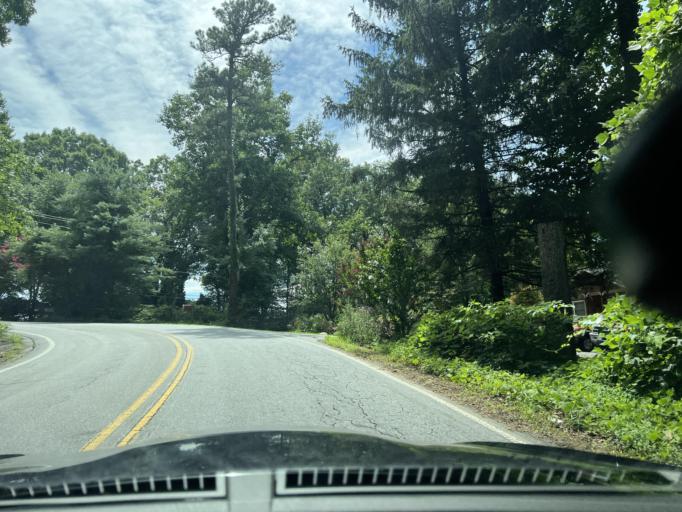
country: US
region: North Carolina
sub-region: Henderson County
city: Edneyville
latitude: 35.3846
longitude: -82.3224
